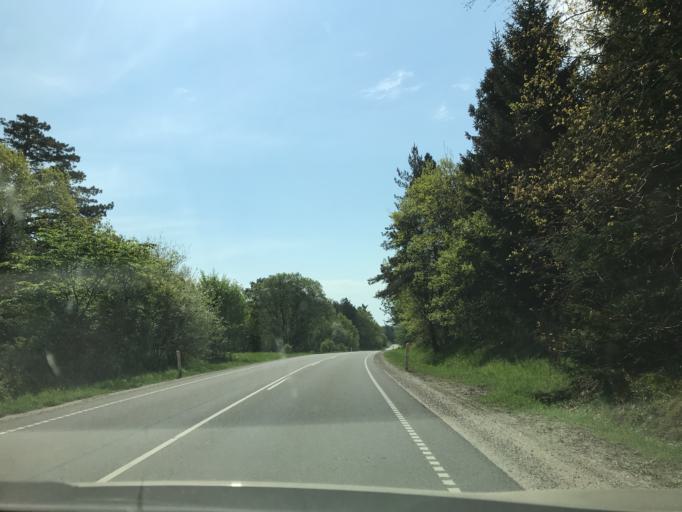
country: DK
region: South Denmark
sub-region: Middelfart Kommune
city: Ejby
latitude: 55.3913
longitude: 9.9130
